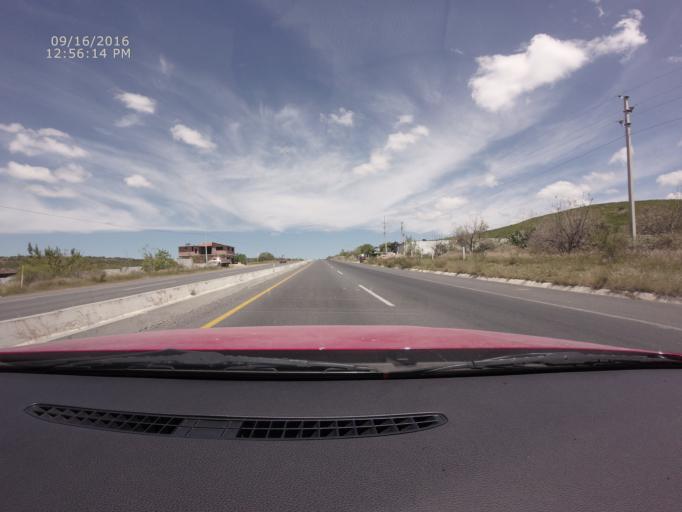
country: MX
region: Queretaro
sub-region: Colon
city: Purisima de Cubos (La Purisima)
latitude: 20.6506
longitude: -100.0991
